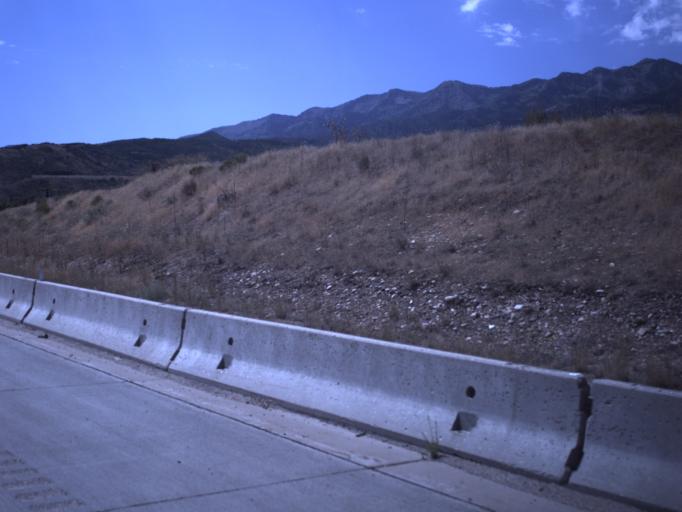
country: US
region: Utah
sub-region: Morgan County
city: Mountain Green
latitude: 41.1217
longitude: -111.7650
